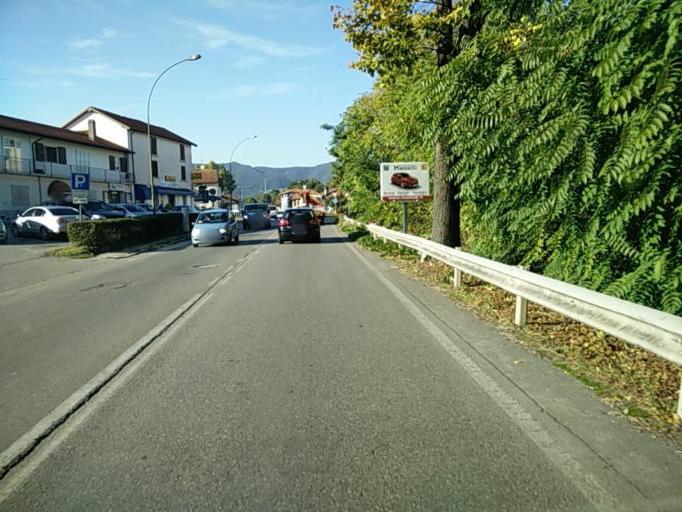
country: IT
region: Lombardy
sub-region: Provincia di Brescia
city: Cunettone-Villa
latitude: 45.5861
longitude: 10.5179
